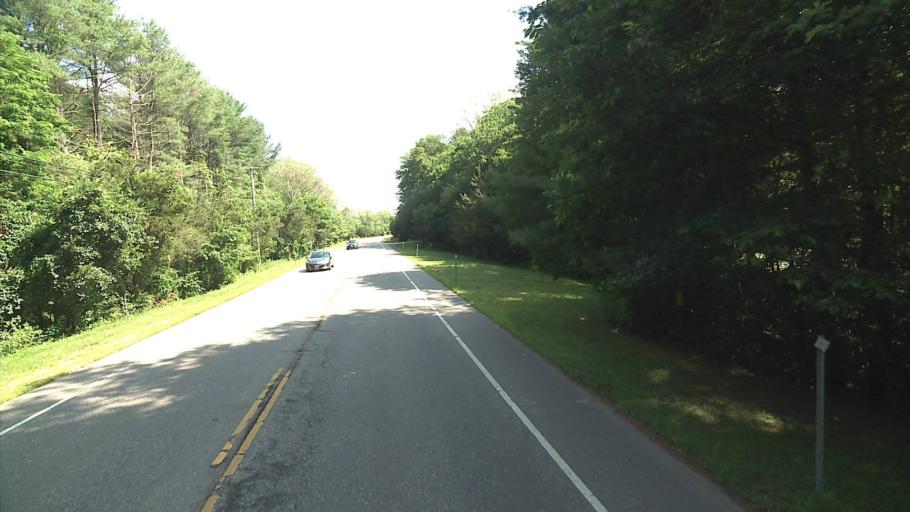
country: US
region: Connecticut
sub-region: Middlesex County
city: Westbrook Center
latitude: 41.3150
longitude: -72.4339
